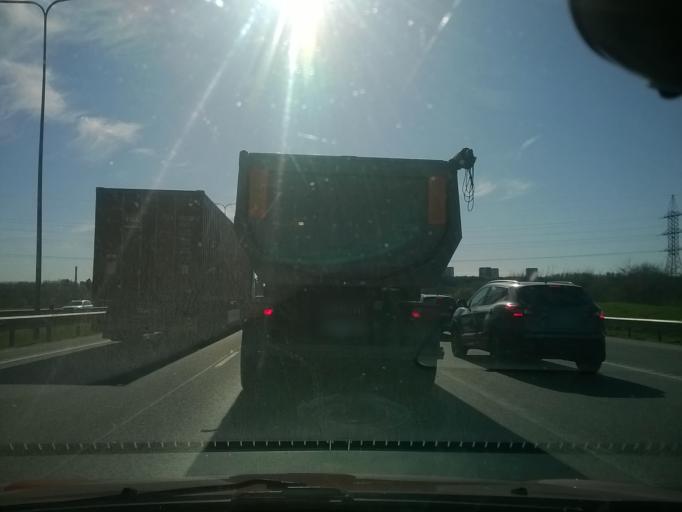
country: EE
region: Harju
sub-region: Joelaehtme vald
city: Loo
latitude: 59.4462
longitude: 24.9228
